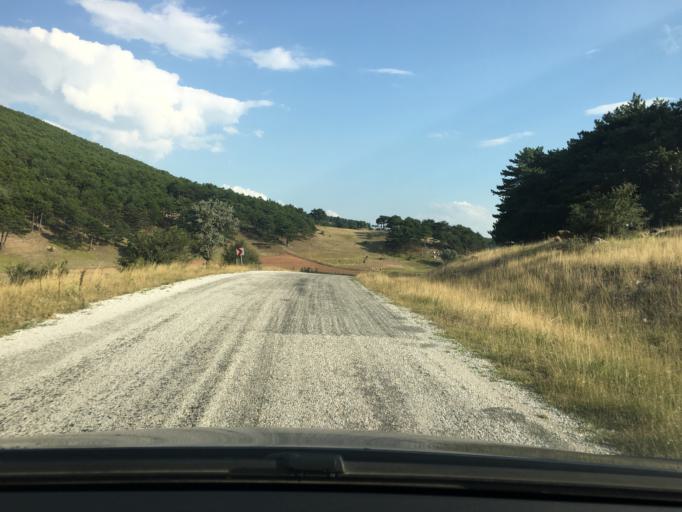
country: TR
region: Eskisehir
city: Kirka
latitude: 39.2956
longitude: 30.6745
